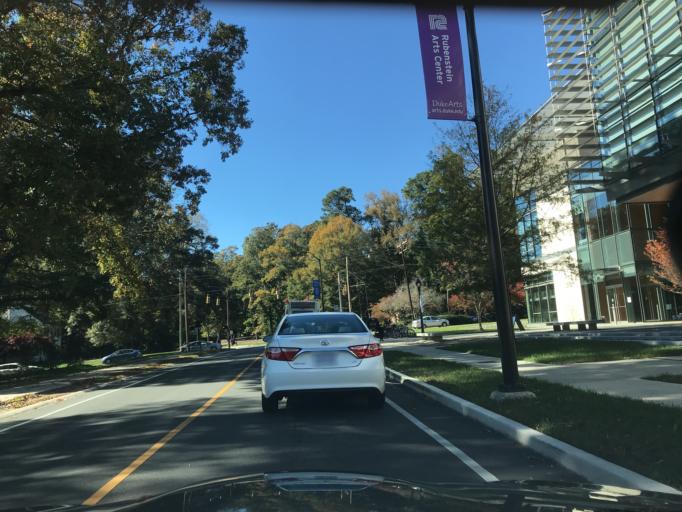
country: US
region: North Carolina
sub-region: Durham County
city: Durham
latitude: 36.0000
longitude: -78.9294
